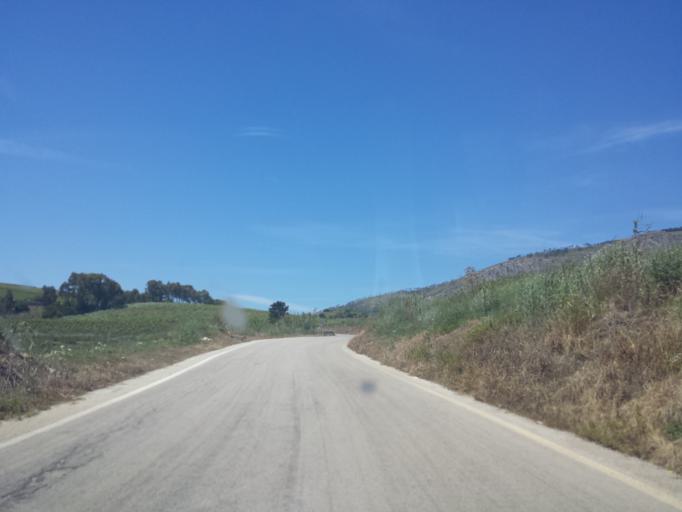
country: IT
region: Sicily
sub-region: Trapani
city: Alcamo
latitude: 37.9702
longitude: 12.9053
